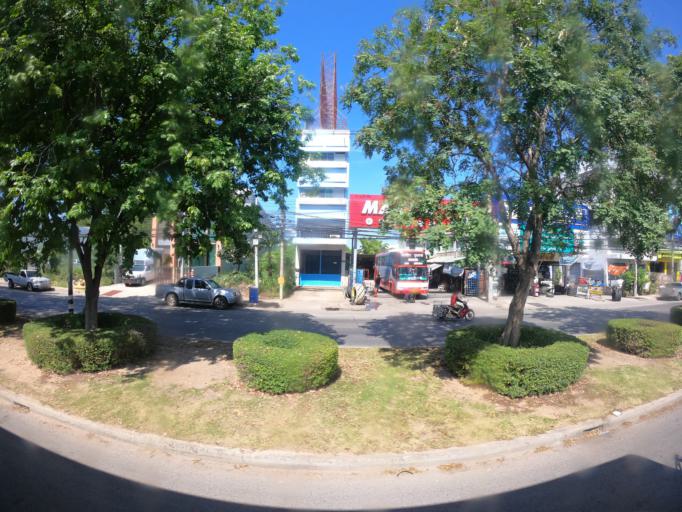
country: TH
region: Nakhon Ratchasima
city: Nakhon Ratchasima
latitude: 14.9908
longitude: 102.0976
